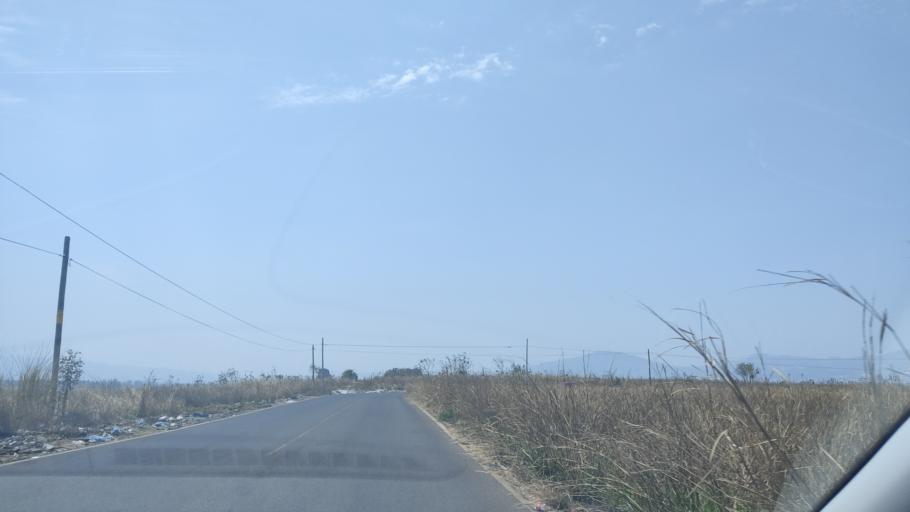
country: MX
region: Nayarit
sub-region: Tepic
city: La Corregidora
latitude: 21.4886
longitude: -104.8048
